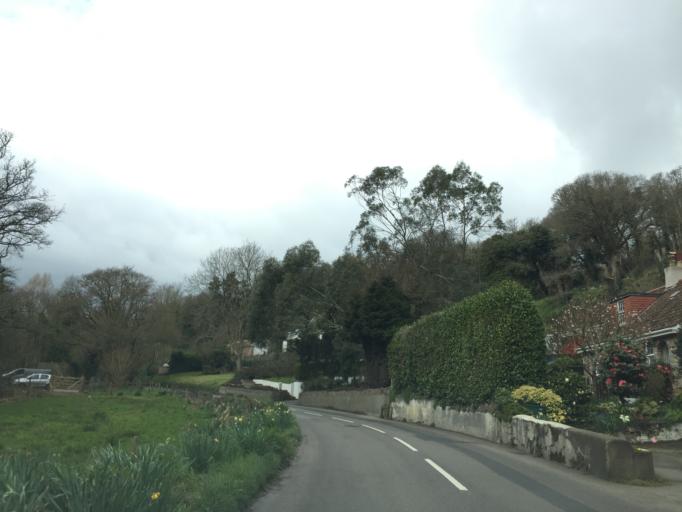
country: JE
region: St Helier
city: Saint Helier
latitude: 49.2121
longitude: -2.1638
